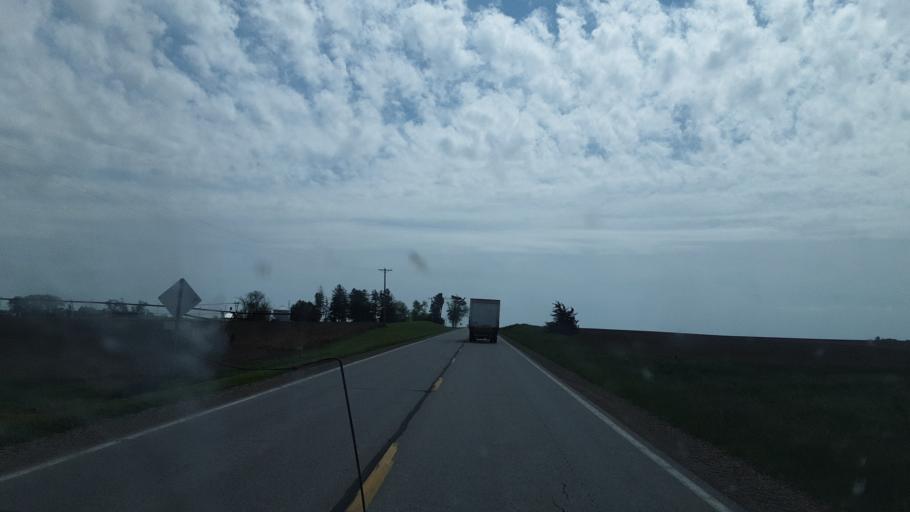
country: US
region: Illinois
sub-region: Logan County
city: Atlanta
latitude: 40.3111
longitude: -89.2324
